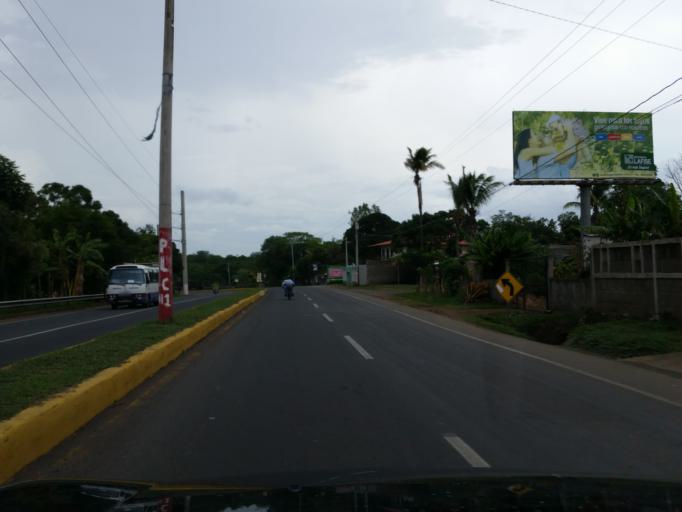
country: NI
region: Masaya
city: Masaya
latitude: 11.9762
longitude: -86.0453
